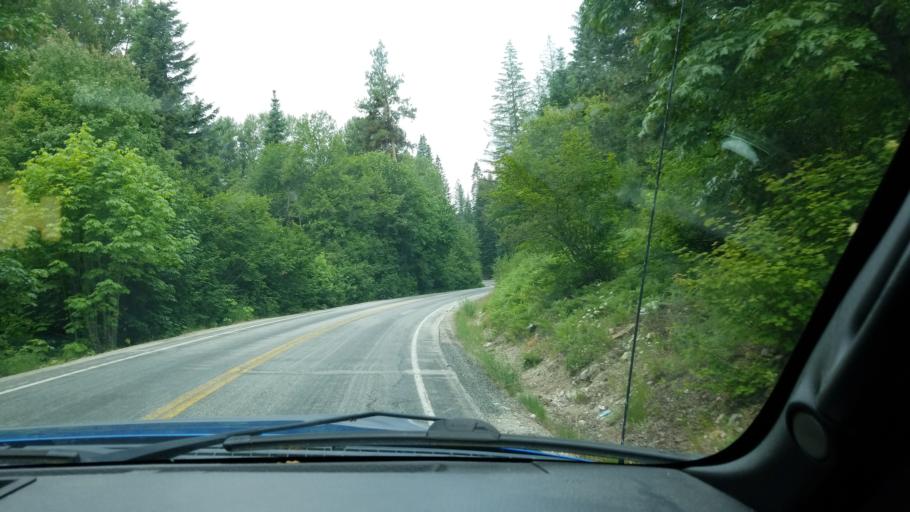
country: US
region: Washington
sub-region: Chelan County
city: Leavenworth
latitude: 47.8473
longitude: -120.8272
